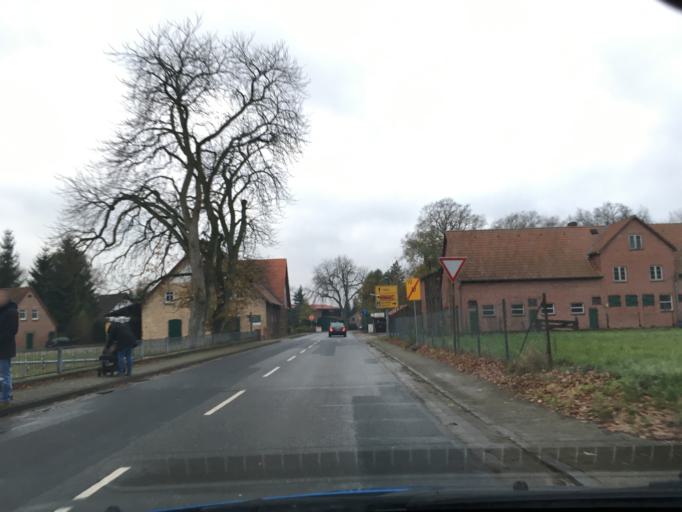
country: DE
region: Lower Saxony
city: Egestorf
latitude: 53.1515
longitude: 10.0689
